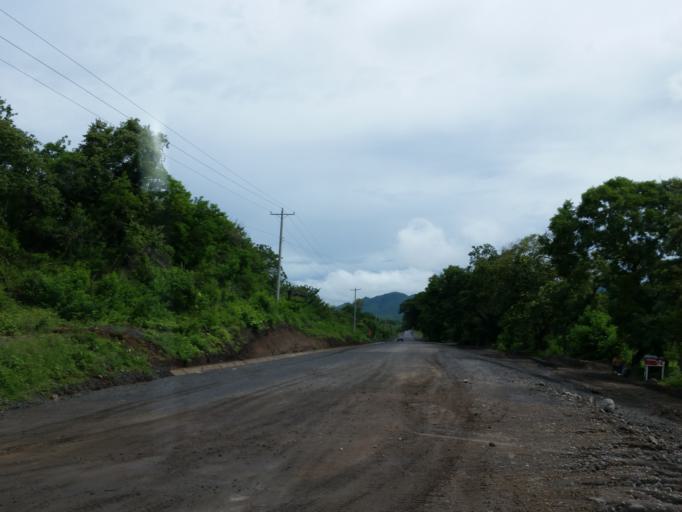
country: NI
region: Leon
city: La Paz Centro
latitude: 12.4196
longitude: -86.6442
